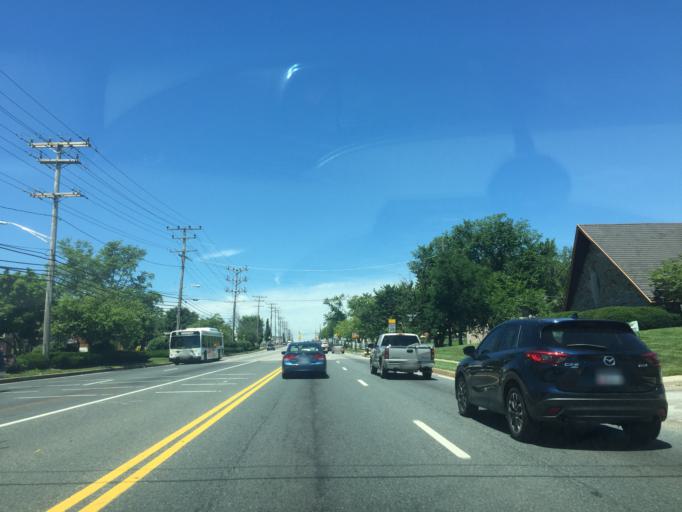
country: US
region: Maryland
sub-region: Baltimore County
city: Milford Mill
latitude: 39.3511
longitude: -76.7506
